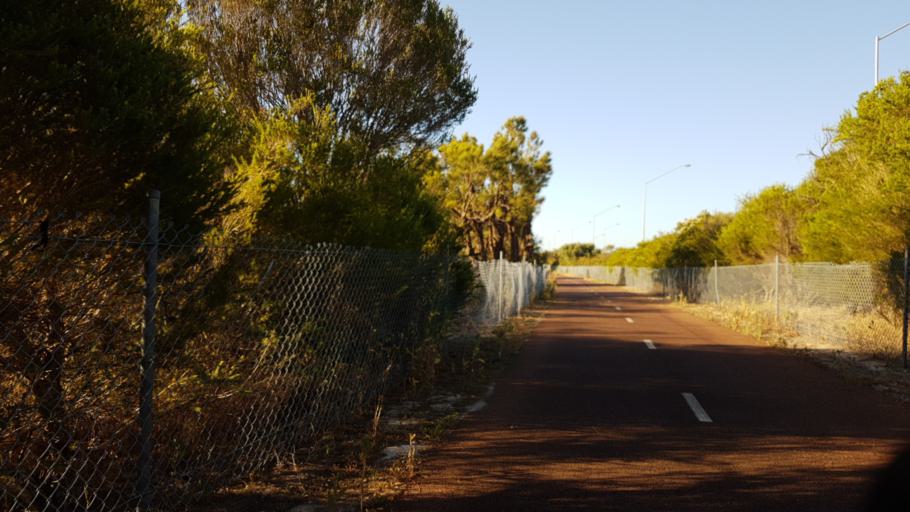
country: AU
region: Western Australia
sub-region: Kwinana
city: Bertram
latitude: -32.2359
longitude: 115.8504
